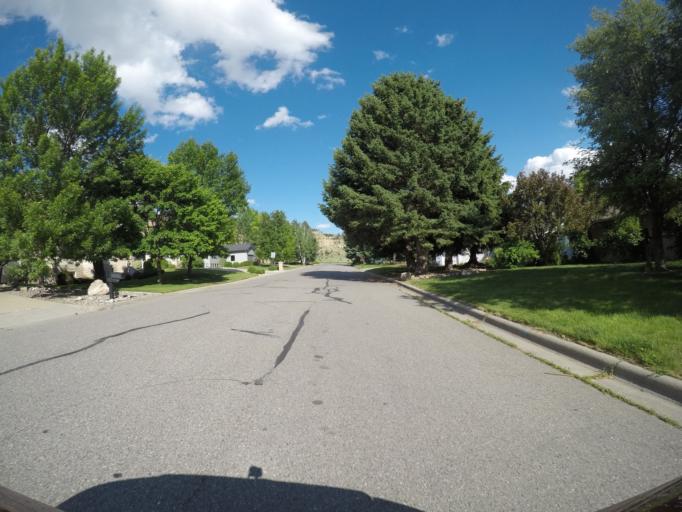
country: US
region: Montana
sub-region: Yellowstone County
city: Billings
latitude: 45.8082
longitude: -108.6543
